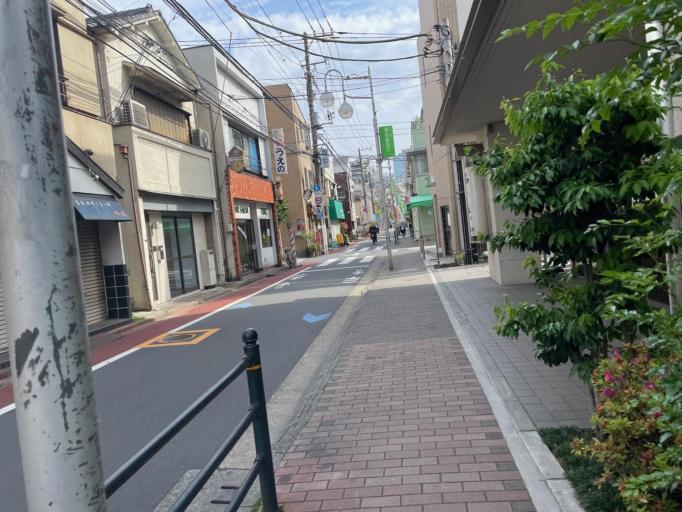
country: JP
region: Kanagawa
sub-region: Kawasaki-shi
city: Kawasaki
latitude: 35.5662
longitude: 139.7205
